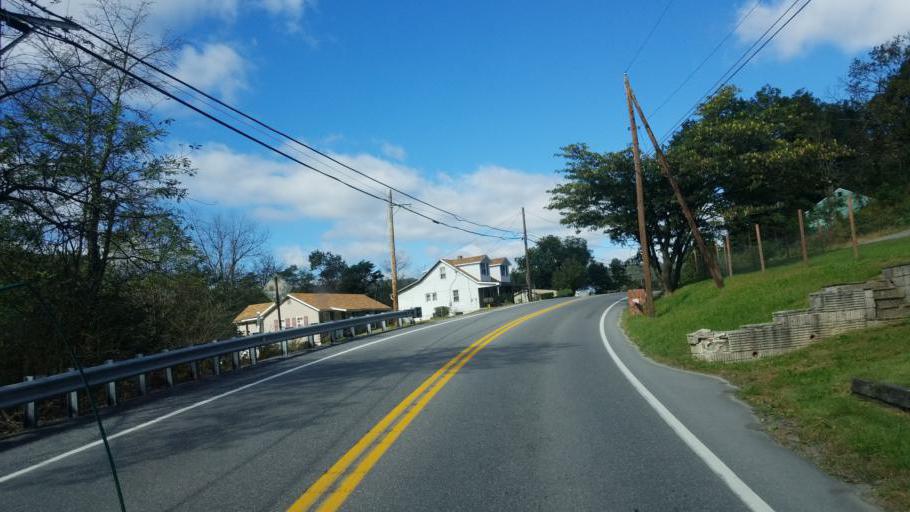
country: US
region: Pennsylvania
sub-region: Fulton County
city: McConnellsburg
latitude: 39.9387
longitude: -78.0180
